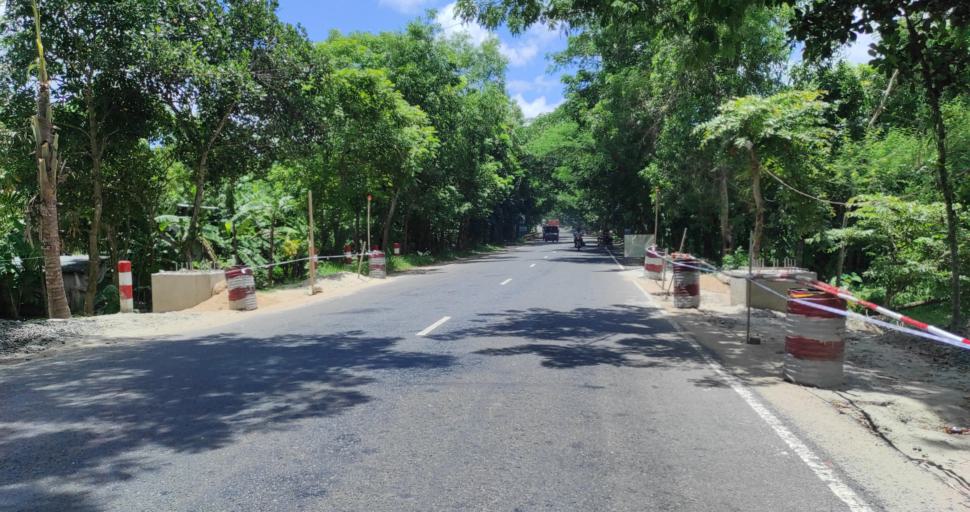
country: BD
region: Barisal
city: Gaurnadi
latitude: 22.8285
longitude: 90.2590
